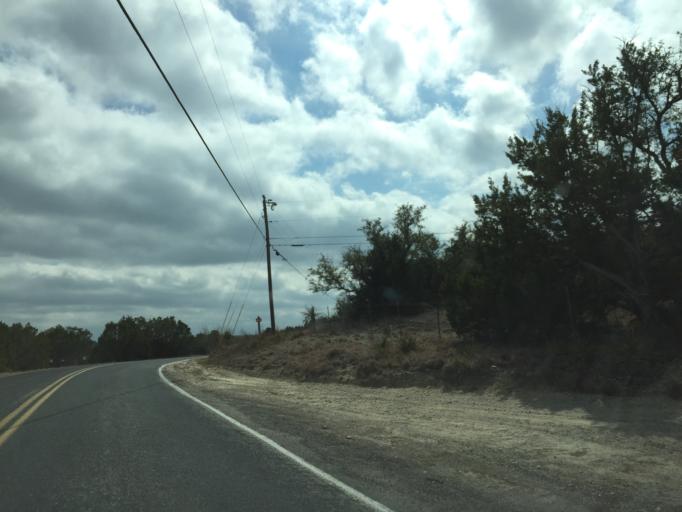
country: US
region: Texas
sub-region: Travis County
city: Briarcliff
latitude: 30.3753
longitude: -98.0926
